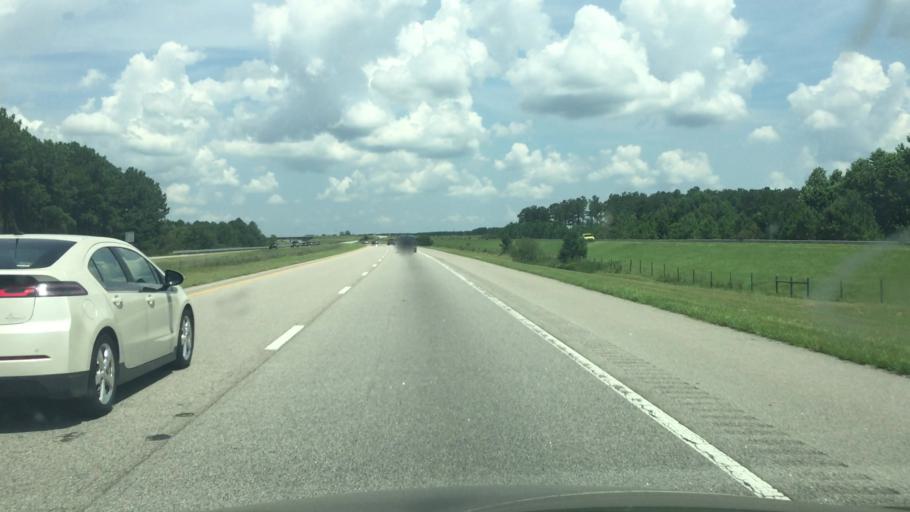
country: US
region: North Carolina
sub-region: Richmond County
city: Ellerbe
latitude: 35.1346
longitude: -79.7142
